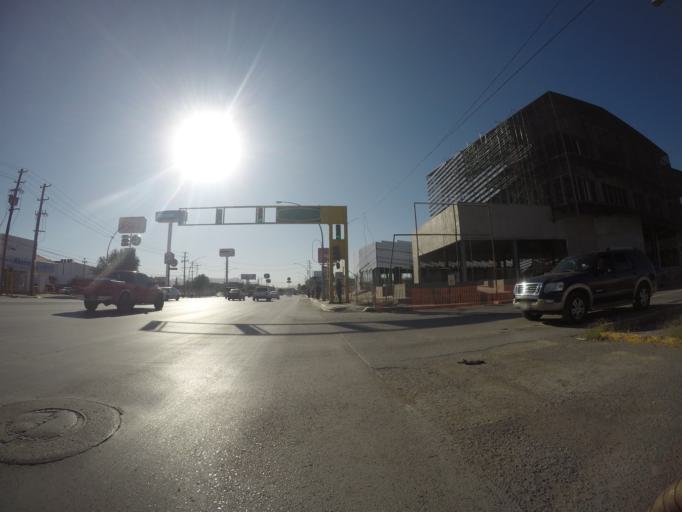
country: MX
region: Chihuahua
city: Ciudad Juarez
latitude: 31.7375
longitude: -106.4426
